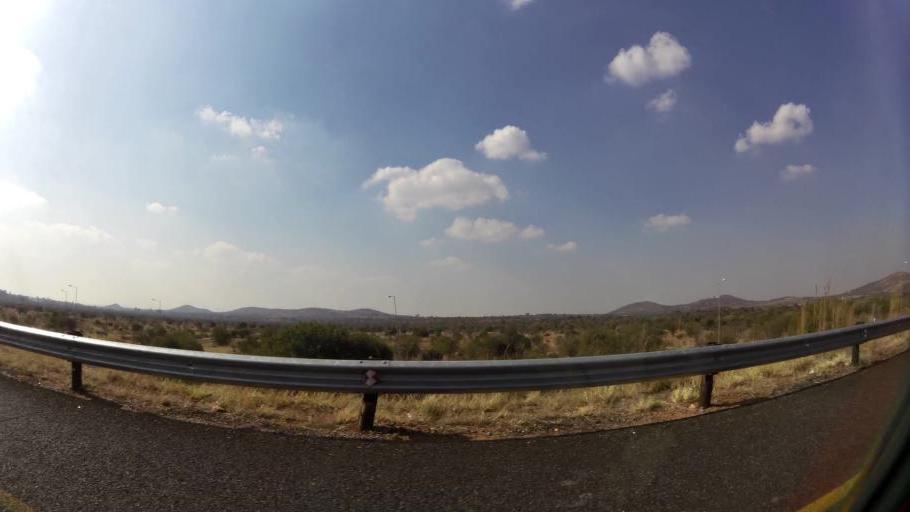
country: ZA
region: North-West
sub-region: Bojanala Platinum District Municipality
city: Rustenburg
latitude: -25.6139
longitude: 27.1533
